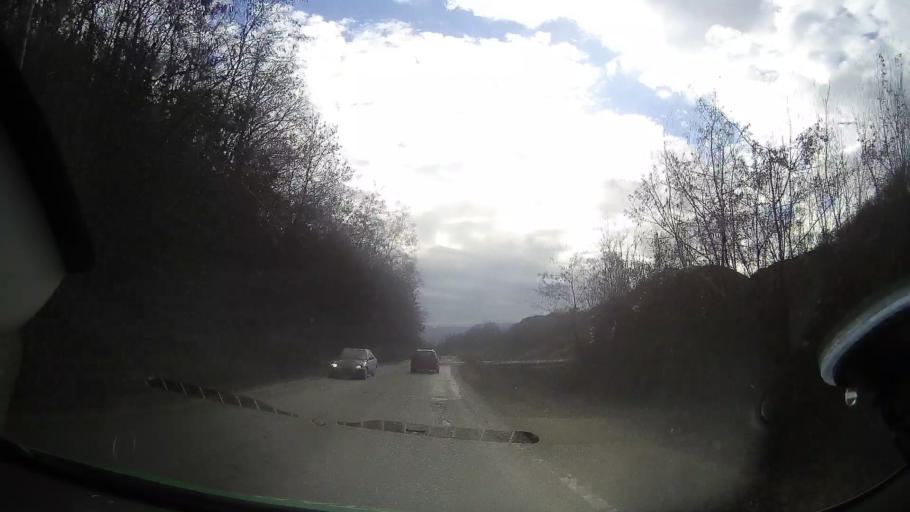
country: RO
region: Cluj
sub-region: Comuna Baisoara
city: Baisoara
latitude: 46.5870
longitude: 23.4589
